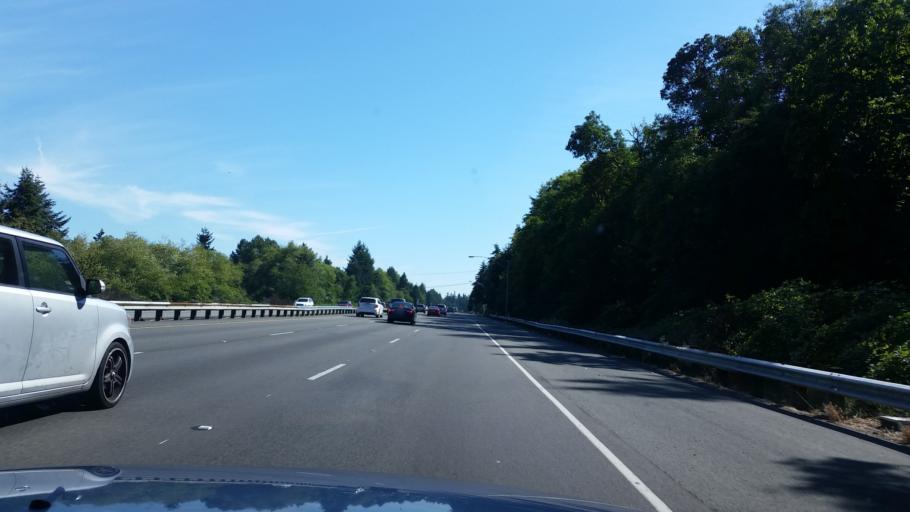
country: US
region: Washington
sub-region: King County
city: Boulevard Park
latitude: 47.5022
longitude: -122.3248
